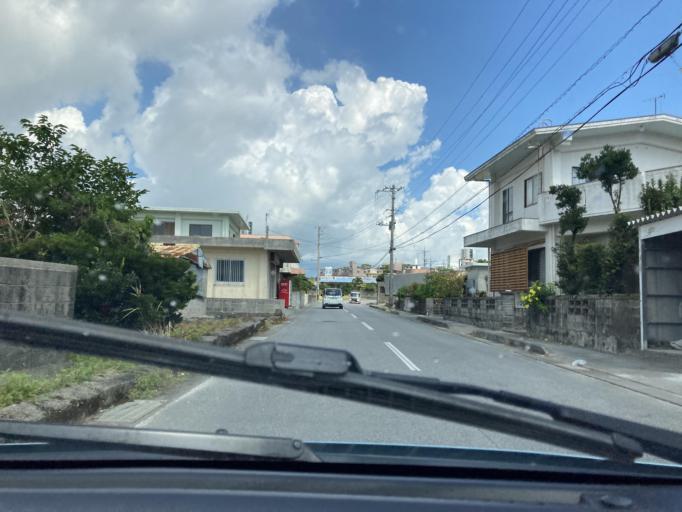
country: JP
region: Okinawa
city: Tomigusuku
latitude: 26.1539
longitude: 127.7541
